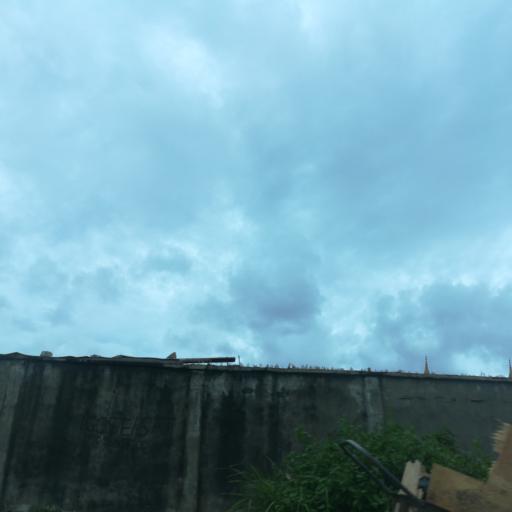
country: NG
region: Lagos
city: Ikoyi
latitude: 6.4392
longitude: 3.4736
